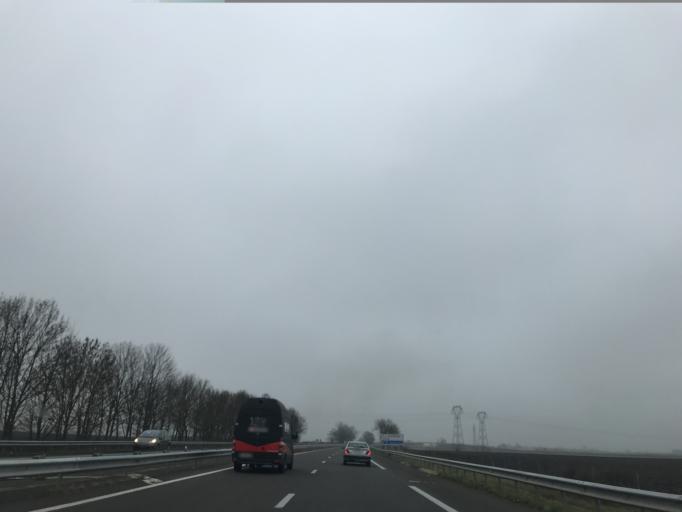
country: FR
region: Auvergne
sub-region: Departement du Puy-de-Dome
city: Pont-du-Chateau
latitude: 45.8129
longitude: 3.2223
